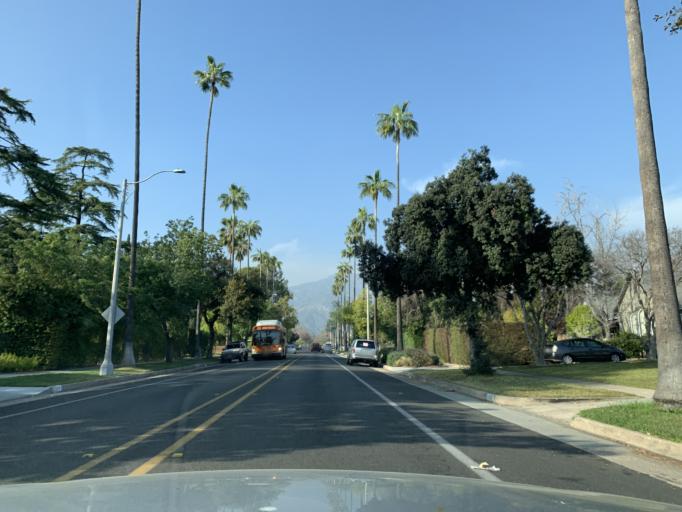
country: US
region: California
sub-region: Los Angeles County
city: Altadena
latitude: 34.1669
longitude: -118.1215
